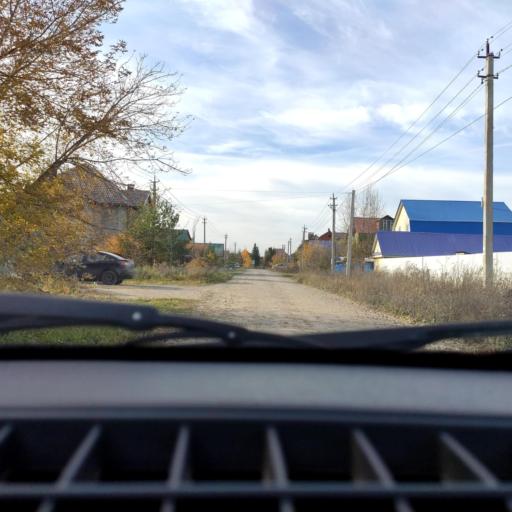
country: RU
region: Bashkortostan
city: Ufa
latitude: 54.6443
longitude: 55.9223
